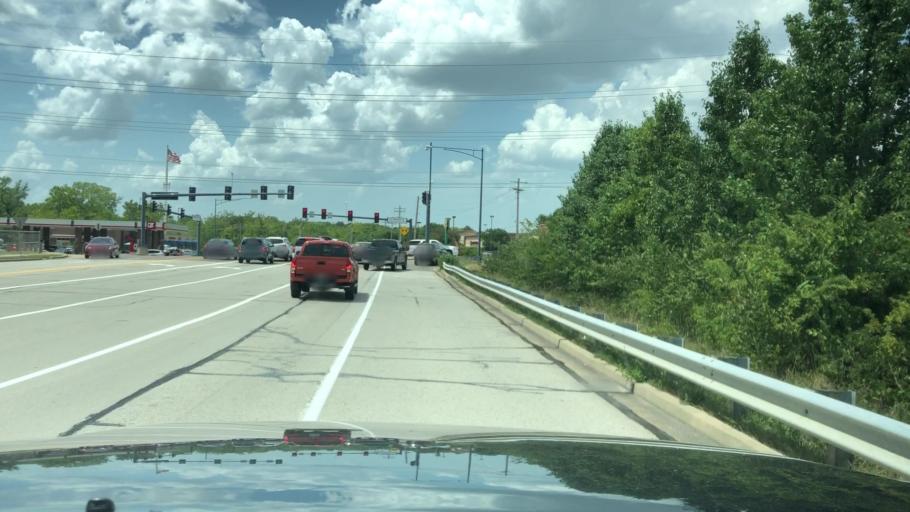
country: US
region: Missouri
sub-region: Saint Charles County
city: O'Fallon
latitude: 38.7924
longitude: -90.6976
